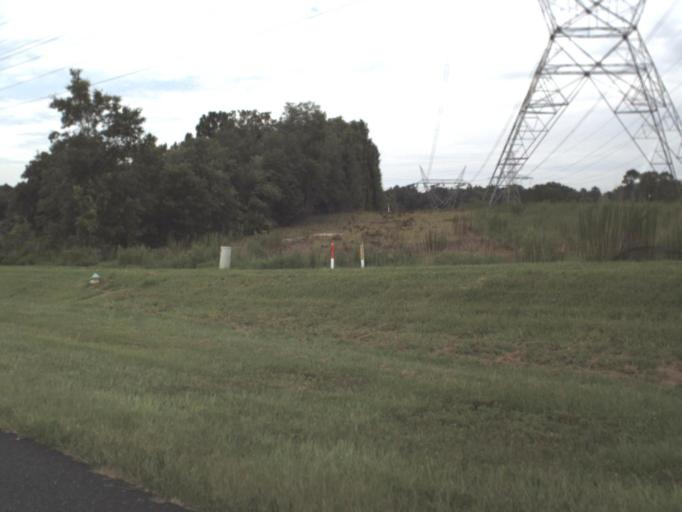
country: US
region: Florida
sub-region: Citrus County
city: Lecanto
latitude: 28.8575
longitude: -82.5018
